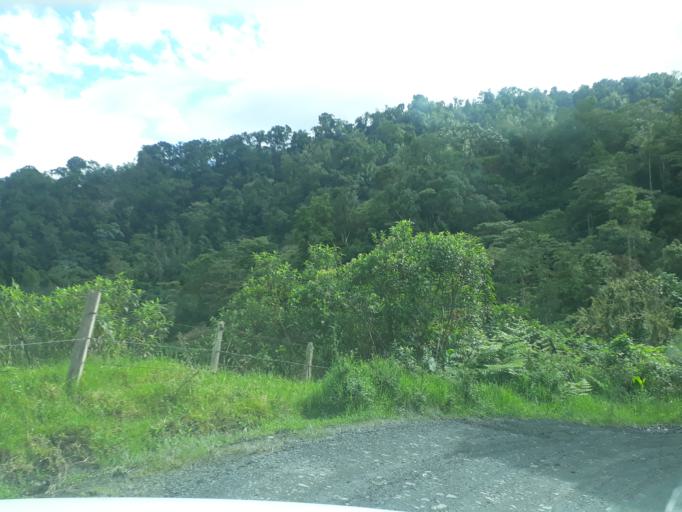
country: CO
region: Cundinamarca
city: Carmen de Carupa
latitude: 5.3425
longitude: -74.0555
